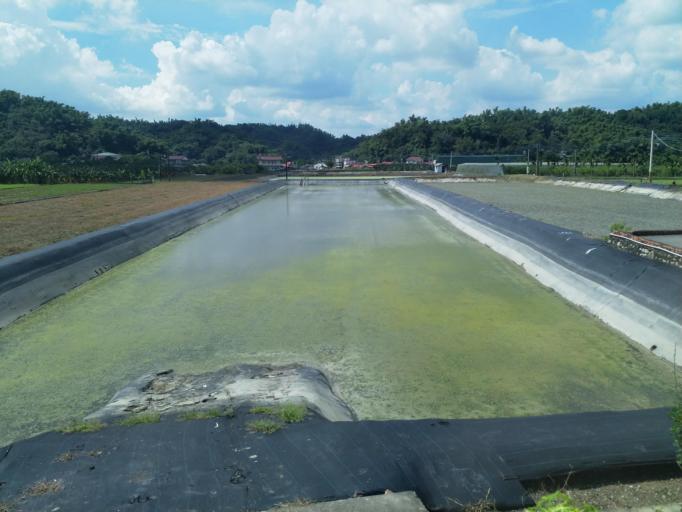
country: TW
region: Taiwan
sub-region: Pingtung
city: Pingtung
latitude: 22.8930
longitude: 120.5797
